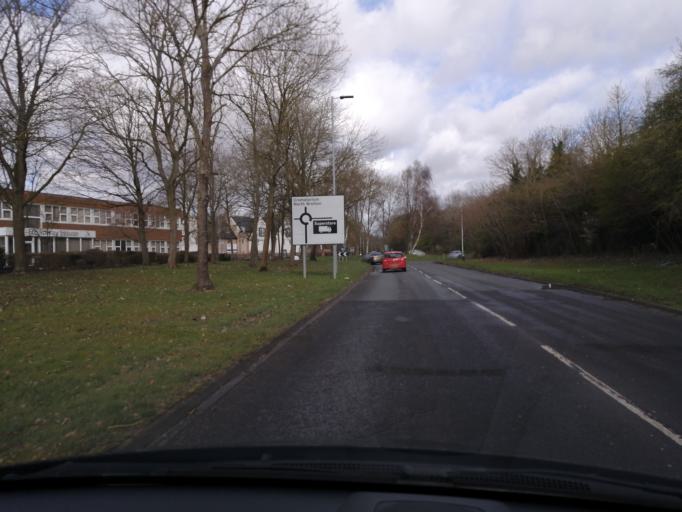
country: GB
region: England
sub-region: Peterborough
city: Marholm
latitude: 52.5911
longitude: -0.2864
